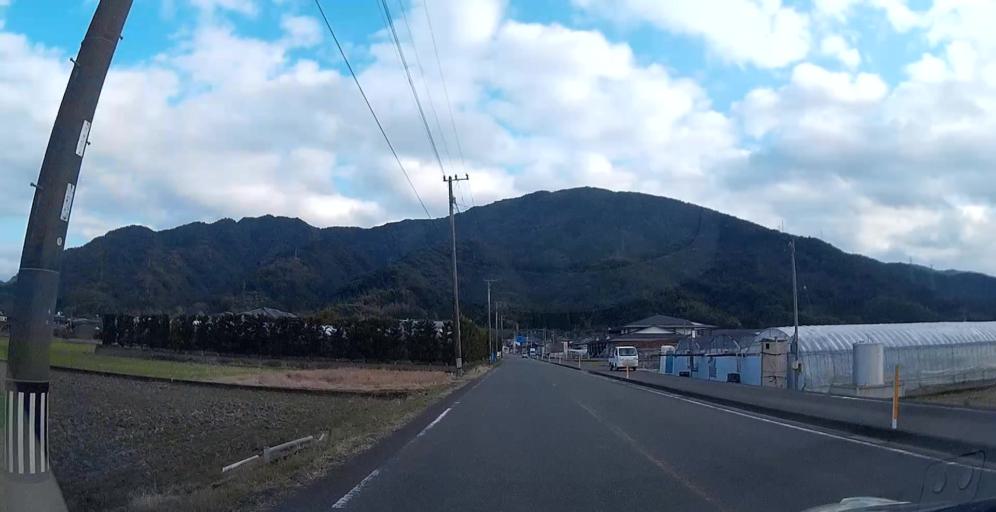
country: JP
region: Kumamoto
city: Yatsushiro
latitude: 32.5291
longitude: 130.6582
